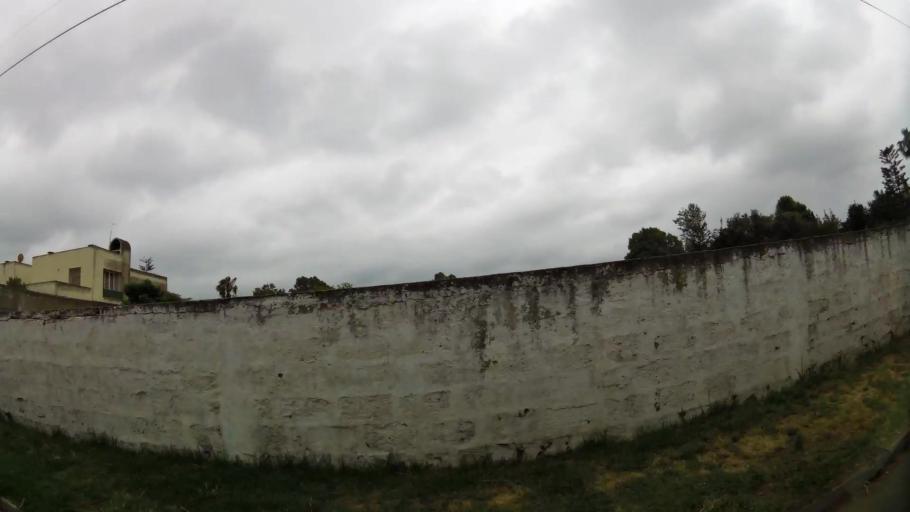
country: MA
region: Rabat-Sale-Zemmour-Zaer
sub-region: Rabat
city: Rabat
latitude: 33.9759
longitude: -6.8282
